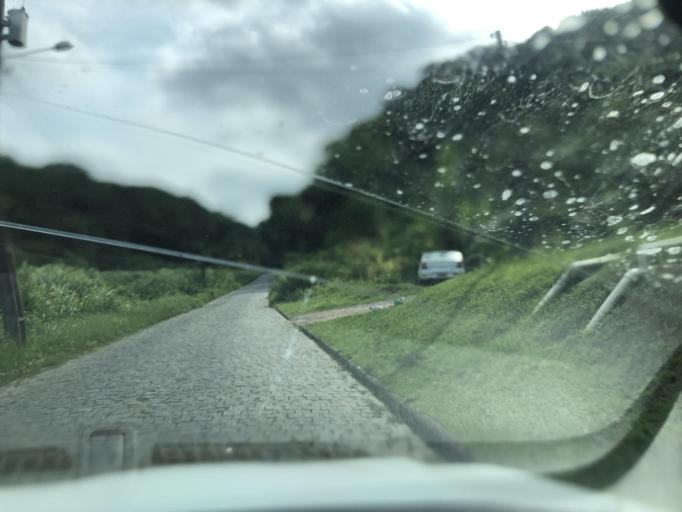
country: BR
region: Santa Catarina
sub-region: Sao Francisco Do Sul
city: Sao Francisco do Sul
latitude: -26.2339
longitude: -48.6269
